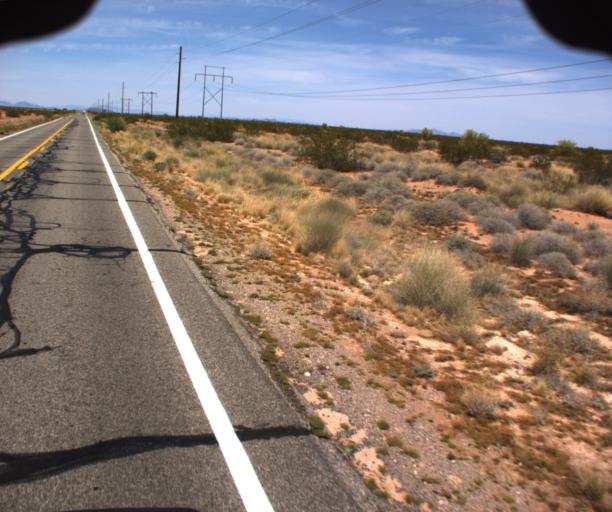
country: US
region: Arizona
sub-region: La Paz County
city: Quartzsite
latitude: 33.8501
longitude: -114.2169
